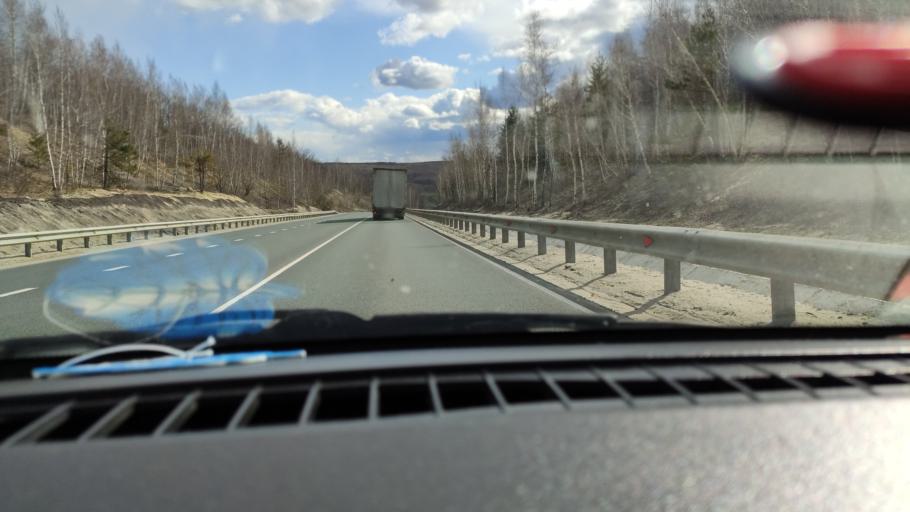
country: RU
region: Saratov
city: Alekseyevka
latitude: 52.4139
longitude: 48.0065
